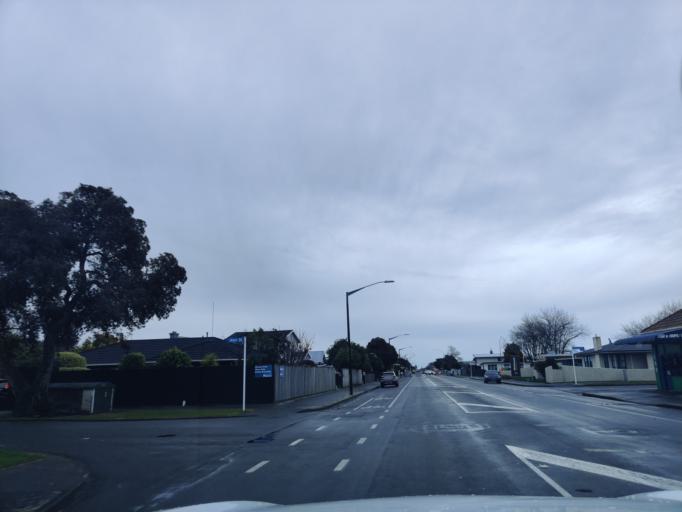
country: NZ
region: Manawatu-Wanganui
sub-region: Palmerston North City
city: Palmerston North
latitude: -40.3458
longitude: 175.6154
